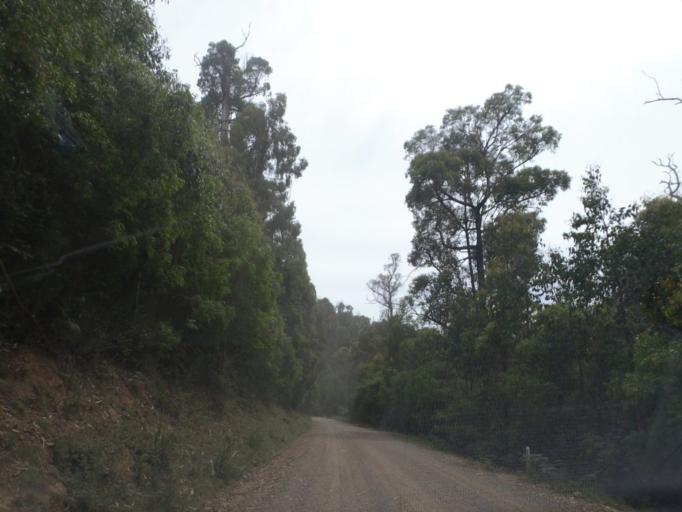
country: AU
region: Victoria
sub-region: Yarra Ranges
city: Healesville
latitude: -37.4538
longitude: 145.5727
